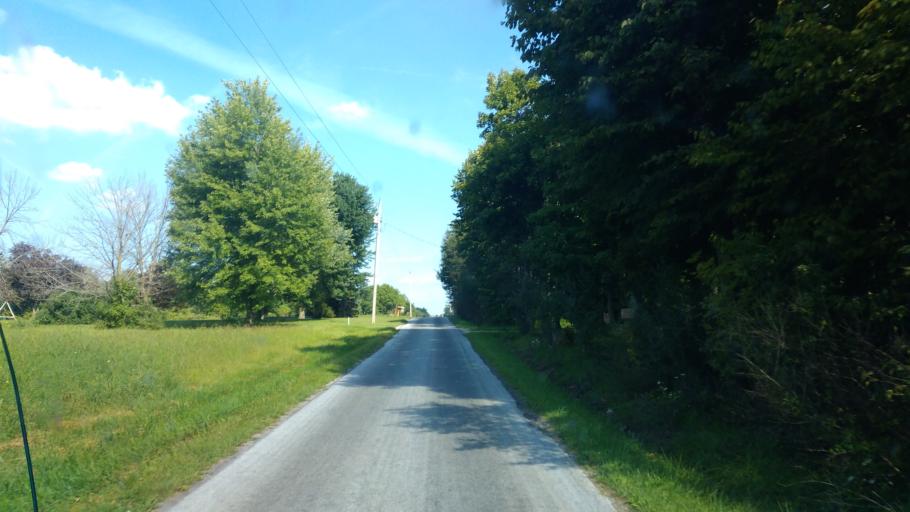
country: US
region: Ohio
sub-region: Hardin County
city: Kenton
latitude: 40.6287
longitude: -83.4652
